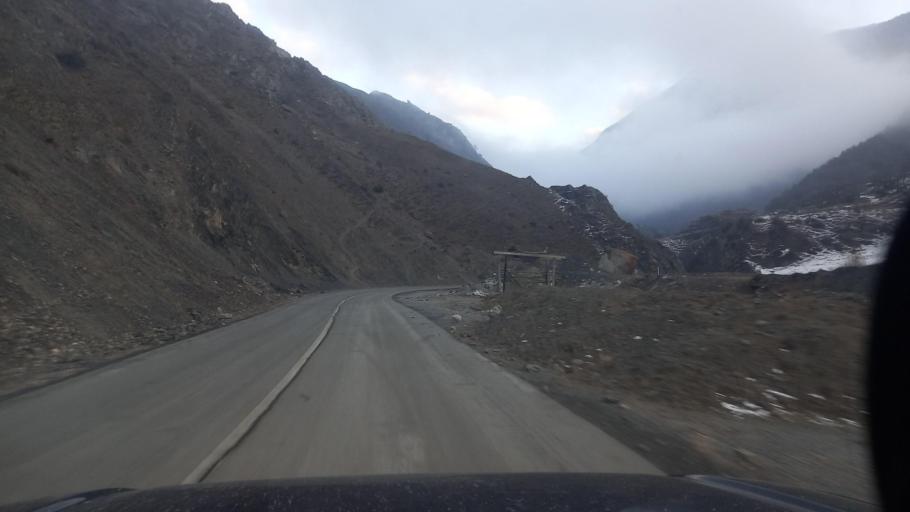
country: RU
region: Ingushetiya
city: Dzhayrakh
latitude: 42.8014
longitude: 44.7575
